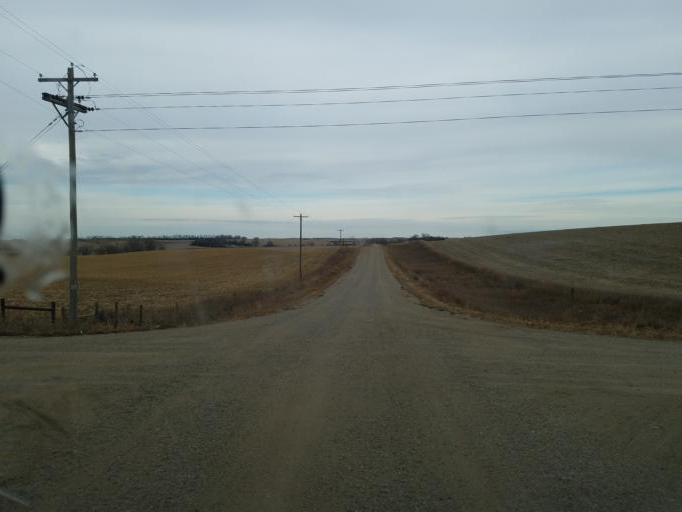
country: US
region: Nebraska
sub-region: Knox County
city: Bloomfield
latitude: 42.5829
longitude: -97.7205
